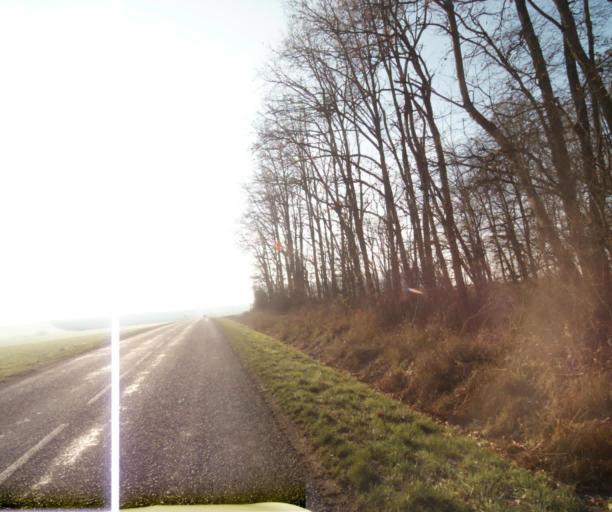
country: FR
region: Champagne-Ardenne
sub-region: Departement de la Haute-Marne
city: Montier-en-Der
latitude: 48.5060
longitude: 4.7485
